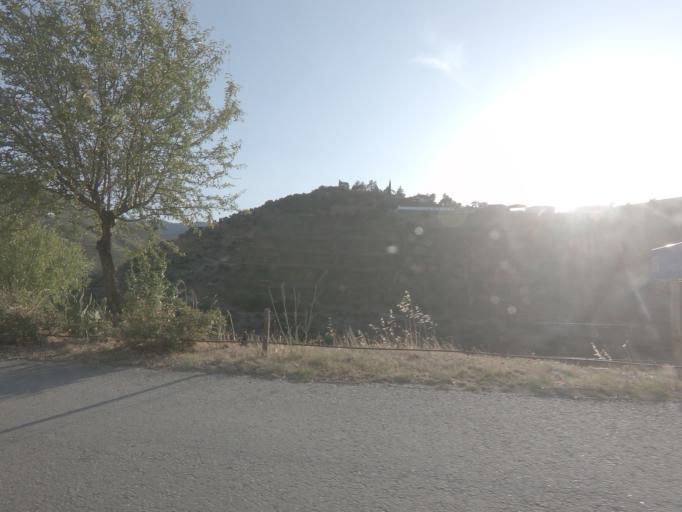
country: PT
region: Vila Real
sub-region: Sabrosa
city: Vilela
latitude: 41.1634
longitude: -7.6243
